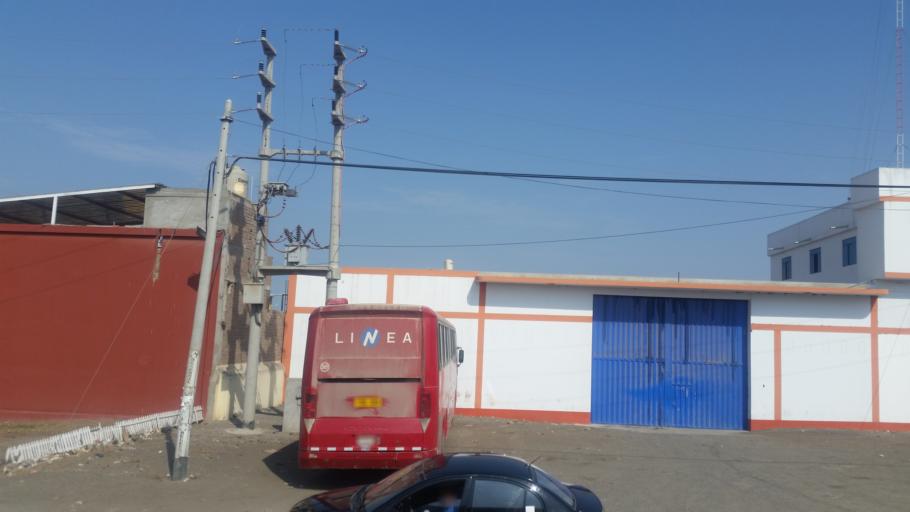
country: PE
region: Lambayeque
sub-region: Provincia de Chiclayo
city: Chiclayo
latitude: -6.8061
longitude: -79.8294
